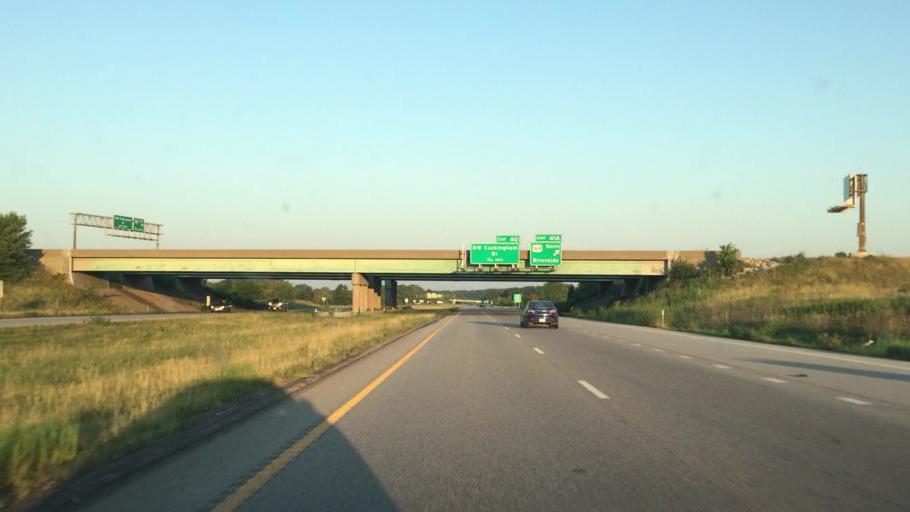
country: US
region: Missouri
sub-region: Clay County
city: Smithville
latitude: 39.3100
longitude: -94.5829
